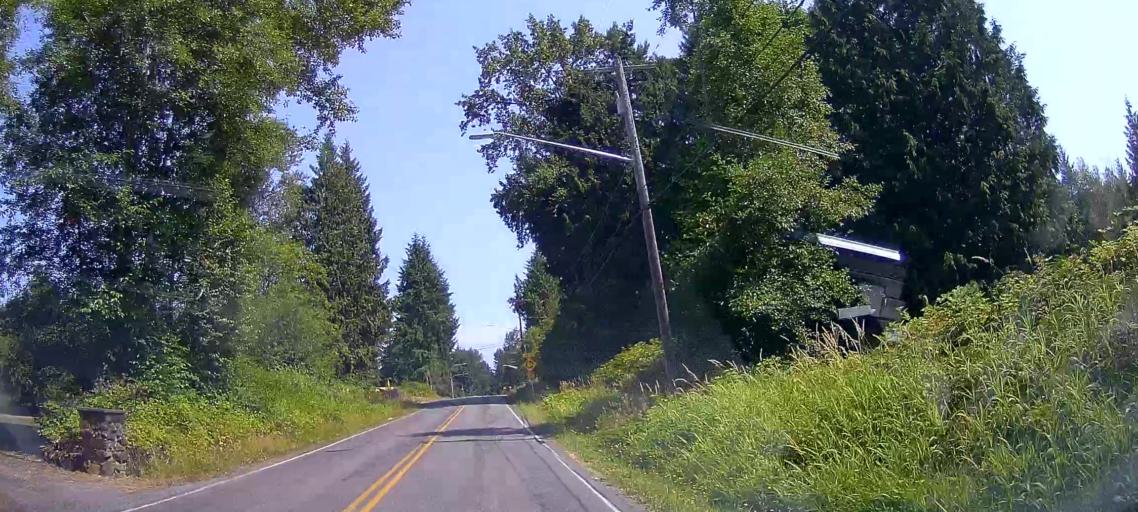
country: US
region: Washington
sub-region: Snohomish County
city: Sisco Heights
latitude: 48.0918
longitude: -122.1145
